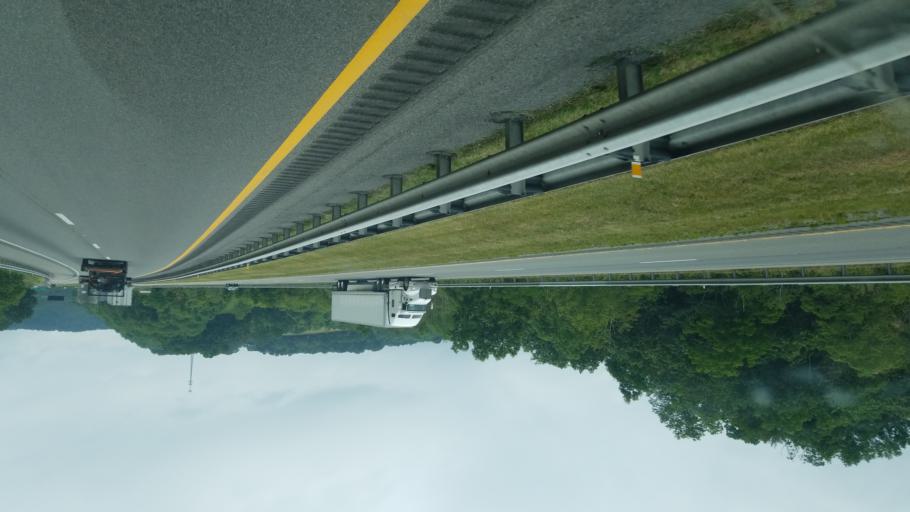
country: US
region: Virginia
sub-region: Wythe County
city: Wytheville
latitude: 37.0054
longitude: -81.0982
